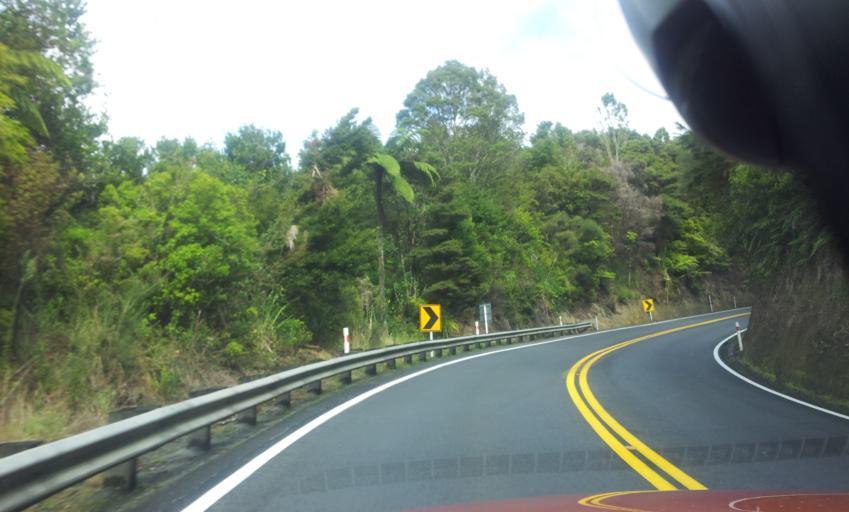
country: NZ
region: Northland
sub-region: Whangarei
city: Ruakaka
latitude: -36.0727
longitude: 174.4198
